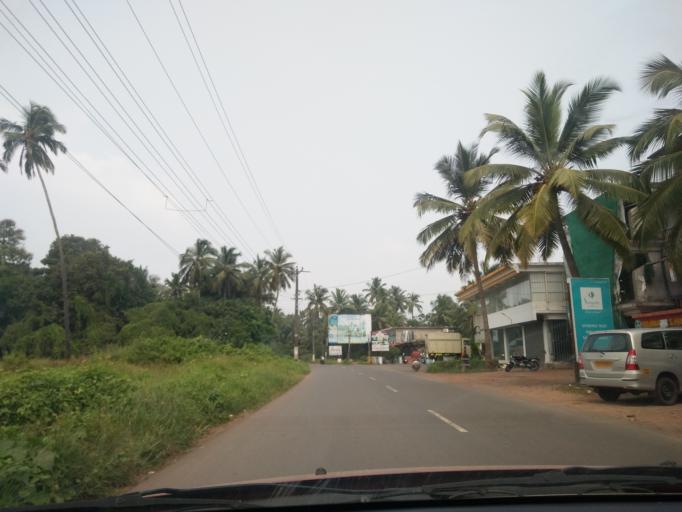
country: IN
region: Goa
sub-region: North Goa
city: Goa Velha
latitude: 15.4247
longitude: 73.8999
